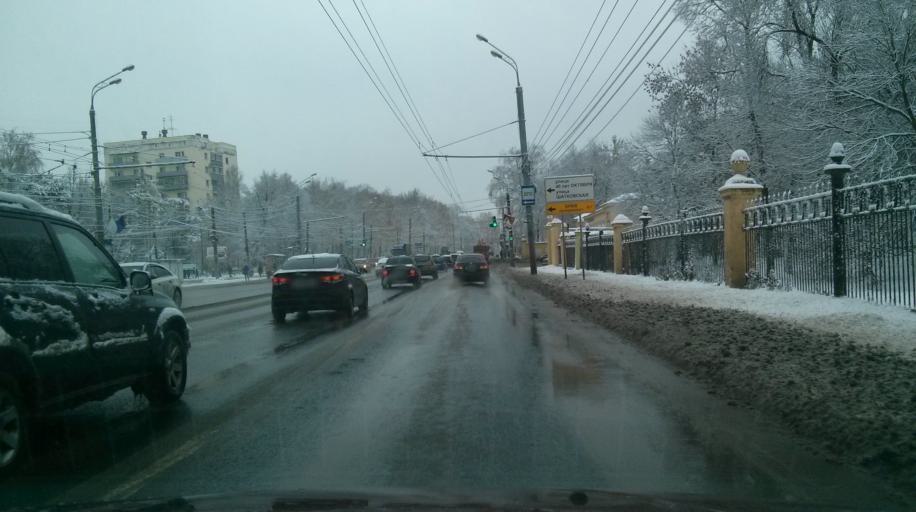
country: RU
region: Nizjnij Novgorod
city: Nizhniy Novgorod
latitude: 56.2626
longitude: 43.9738
